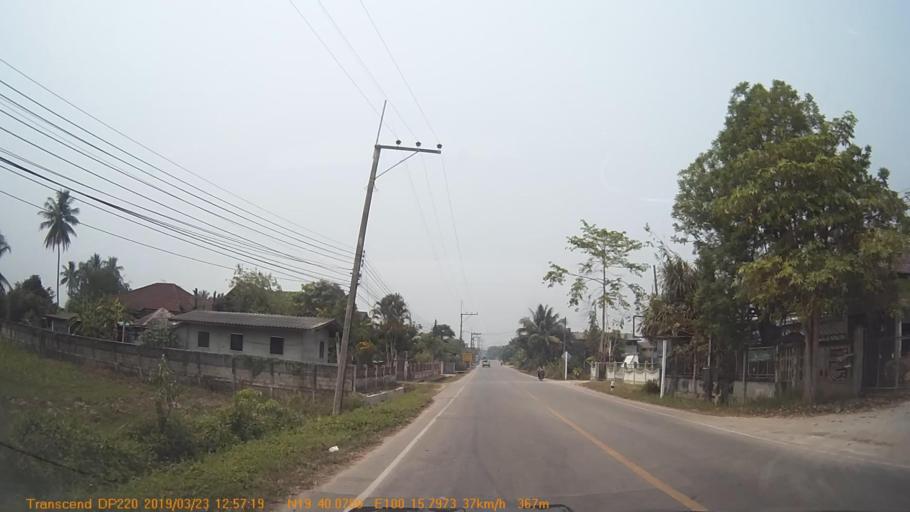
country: TH
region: Chiang Rai
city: Thoeng
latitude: 19.6681
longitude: 100.2632
